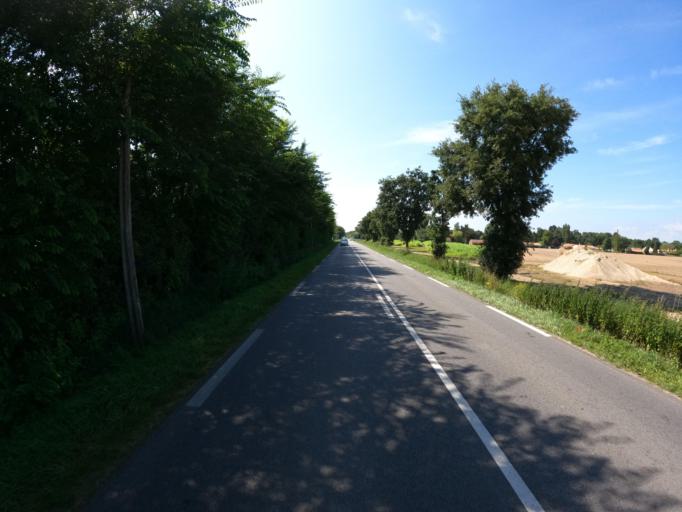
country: FR
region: Pays de la Loire
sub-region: Departement de la Loire-Atlantique
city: Machecoul
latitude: 47.0079
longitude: -1.8452
